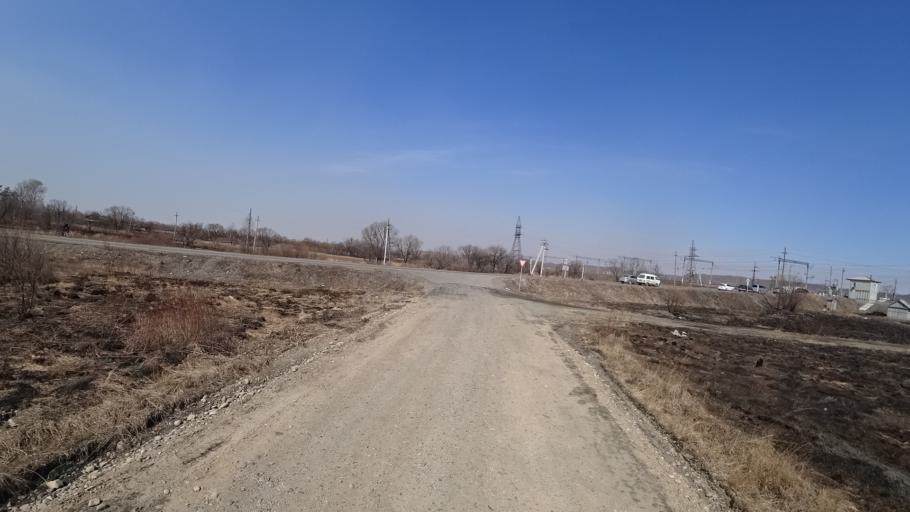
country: RU
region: Amur
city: Novobureyskiy
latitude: 49.7917
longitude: 129.8518
